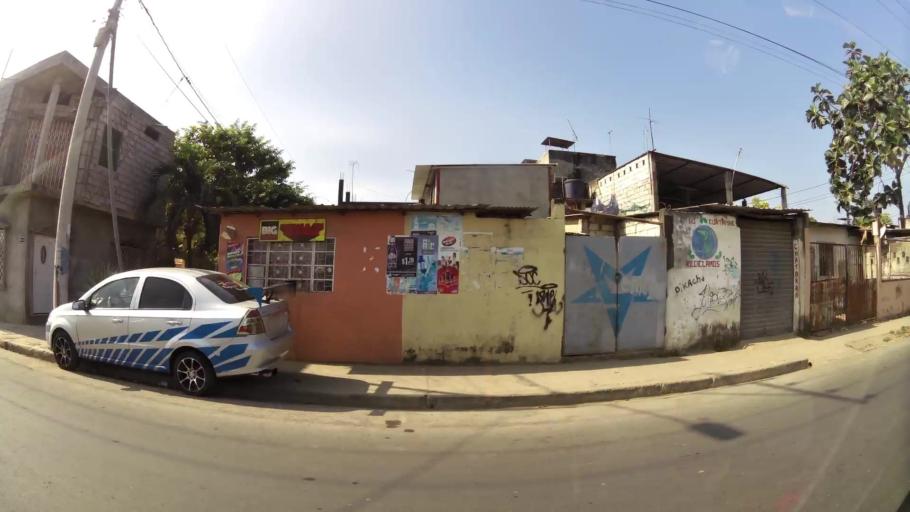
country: EC
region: Guayas
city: Eloy Alfaro
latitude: -2.1646
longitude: -79.7935
